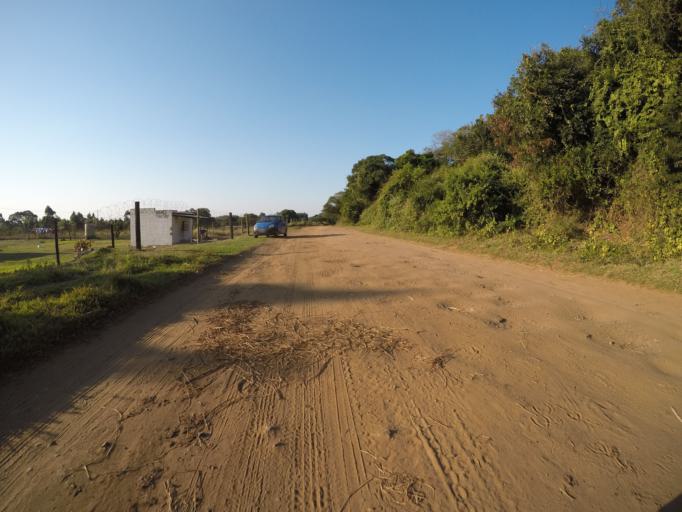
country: ZA
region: KwaZulu-Natal
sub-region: uThungulu District Municipality
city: KwaMbonambi
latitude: -28.7056
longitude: 32.1868
